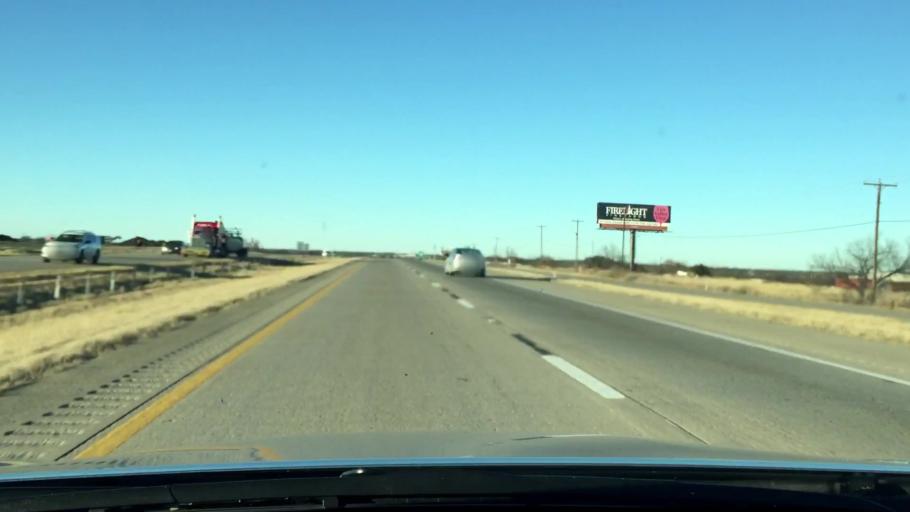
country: US
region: Texas
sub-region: Denton County
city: Sanger
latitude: 33.4533
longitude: -97.1642
